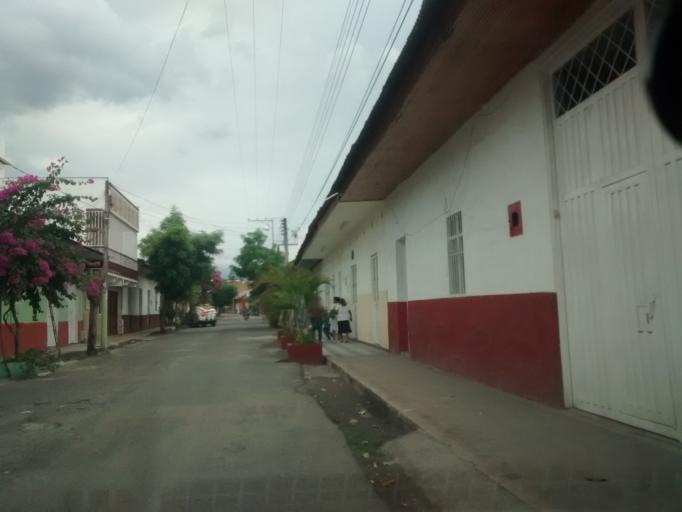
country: CO
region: Cundinamarca
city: Tocaima
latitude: 4.4592
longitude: -74.6330
